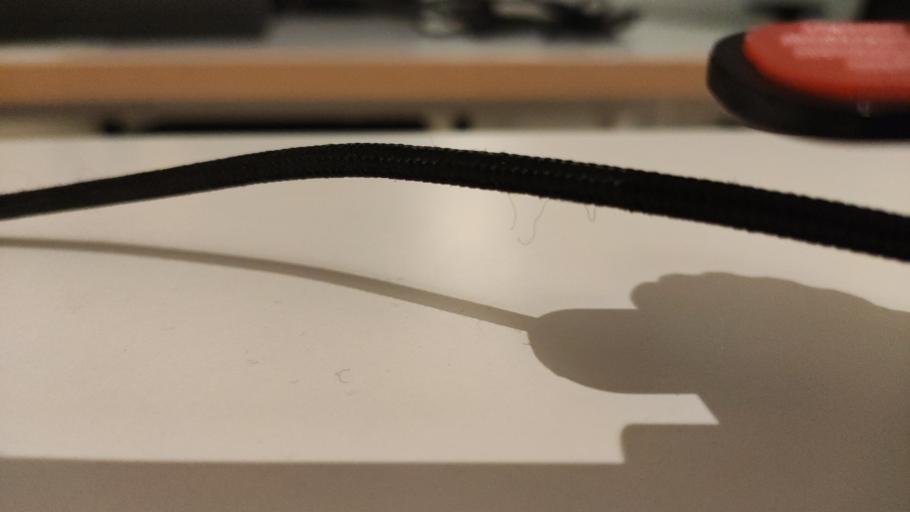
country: RU
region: Moskovskaya
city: Semkhoz
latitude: 56.3833
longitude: 38.0675
